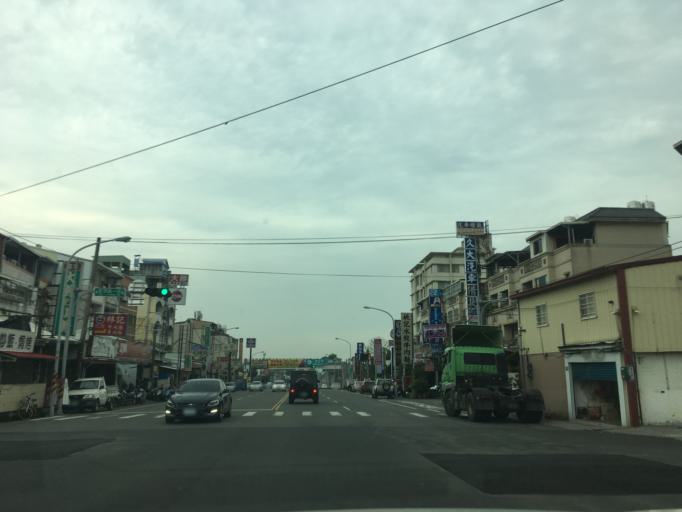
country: TW
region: Taiwan
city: Zhongxing New Village
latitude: 23.9787
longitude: 120.7002
